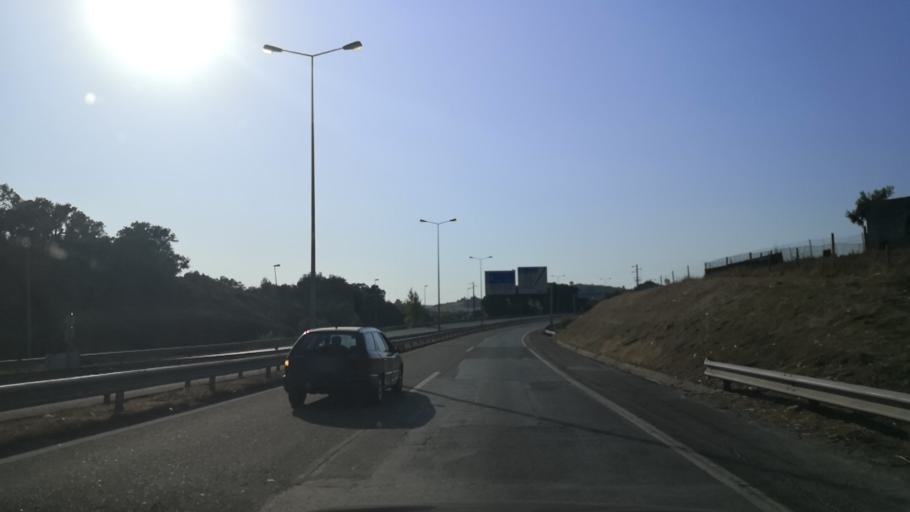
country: PT
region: Santarem
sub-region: Santarem
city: Santarem
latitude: 39.2255
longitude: -8.7003
